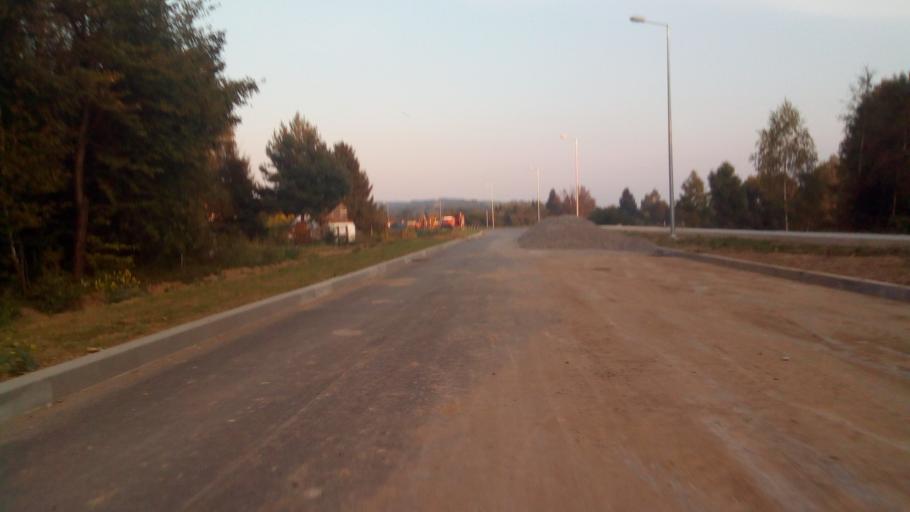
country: PL
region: Subcarpathian Voivodeship
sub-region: Powiat strzyzowski
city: Strzyzow
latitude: 49.8674
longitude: 21.7815
